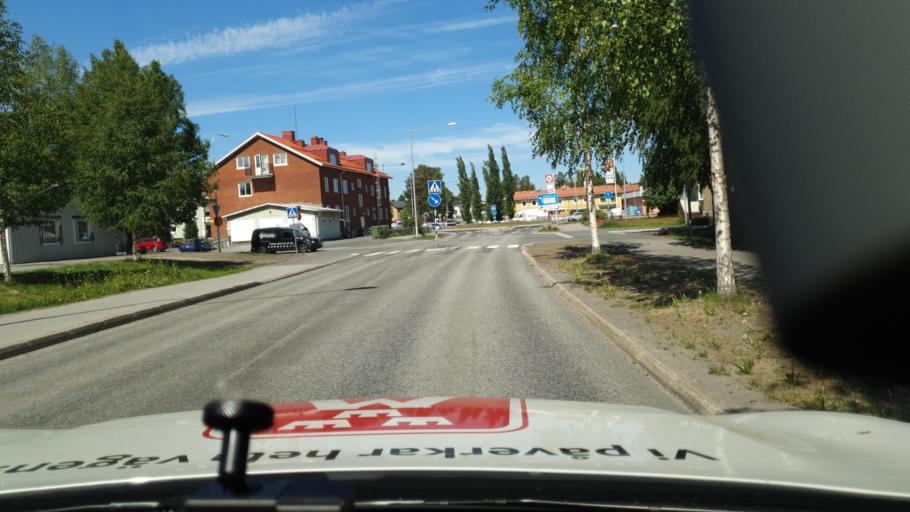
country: SE
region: Vaesterbotten
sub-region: Umea Kommun
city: Umea
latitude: 63.8172
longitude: 20.2414
